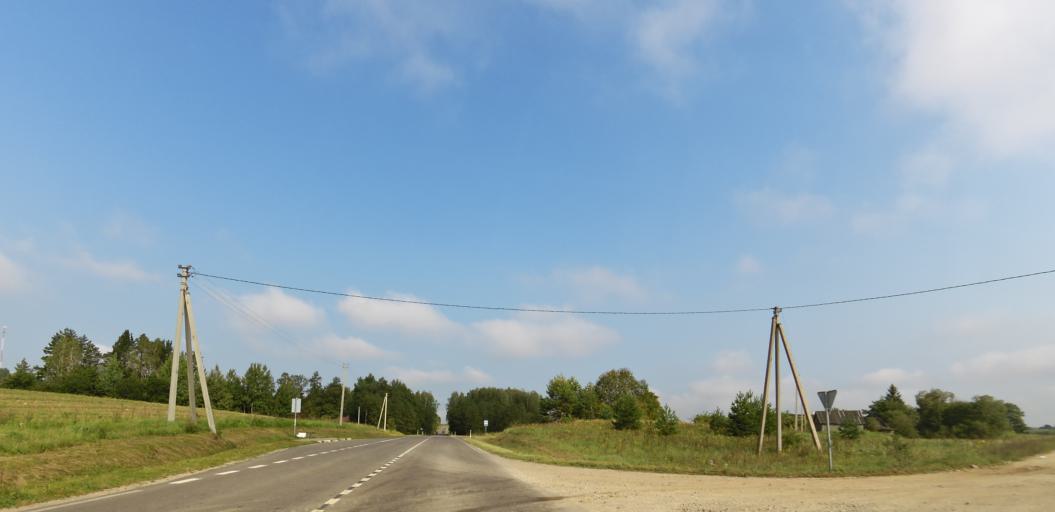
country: LT
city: Grigiskes
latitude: 54.7659
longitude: 25.0803
